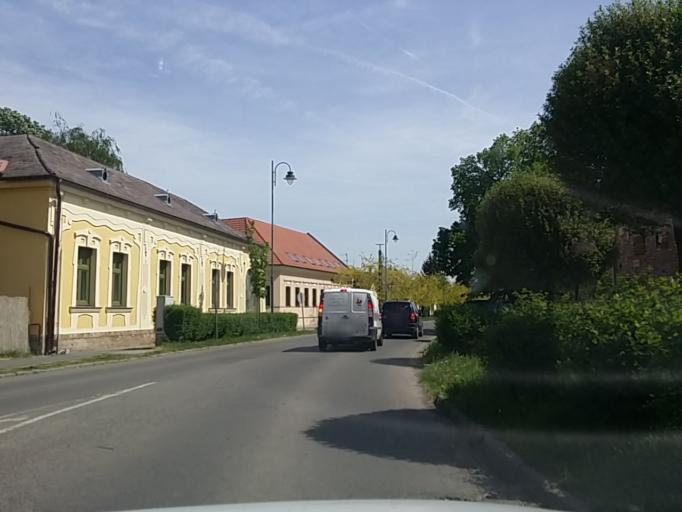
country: HU
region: Bekes
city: Gyula
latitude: 46.6475
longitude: 21.2862
